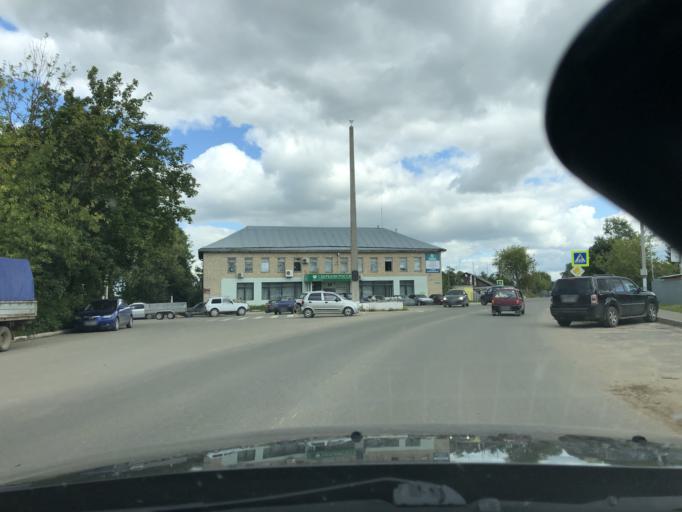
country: RU
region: Tula
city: Yasnogorsk
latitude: 54.4812
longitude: 37.6986
